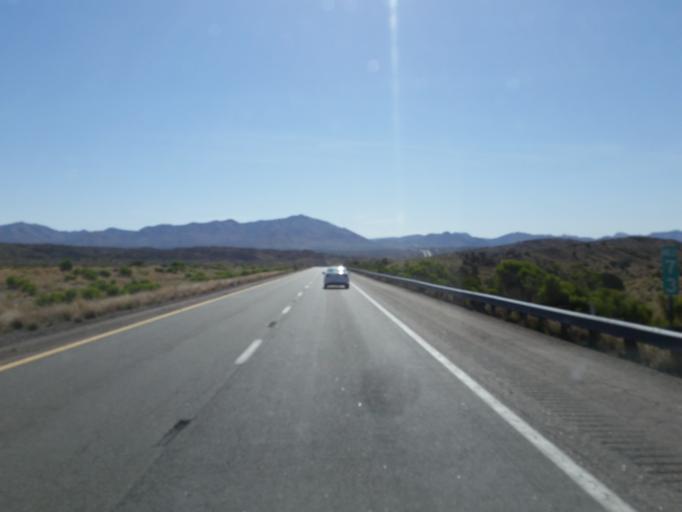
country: US
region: Arizona
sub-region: Mohave County
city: New Kingman-Butler
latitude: 35.1607
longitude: -113.6786
